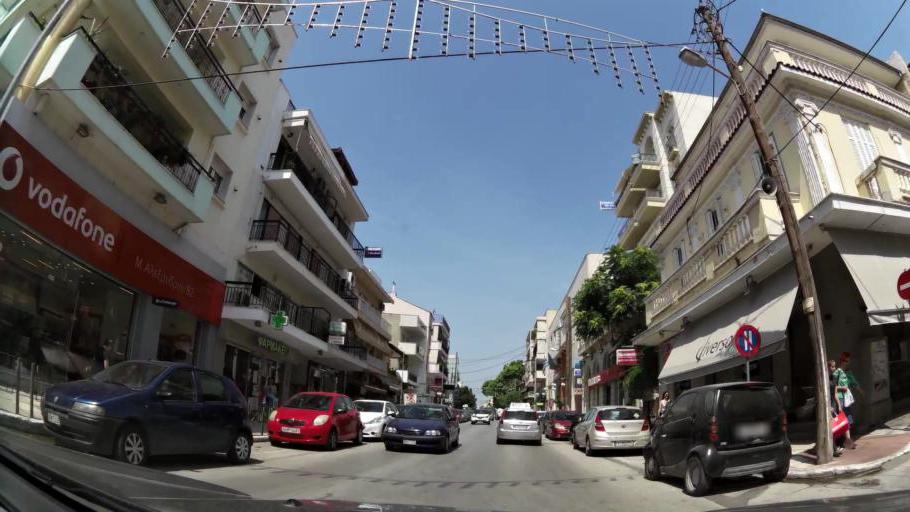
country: GR
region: Central Macedonia
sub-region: Nomos Thessalonikis
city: Evosmos
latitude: 40.6695
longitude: 22.9100
